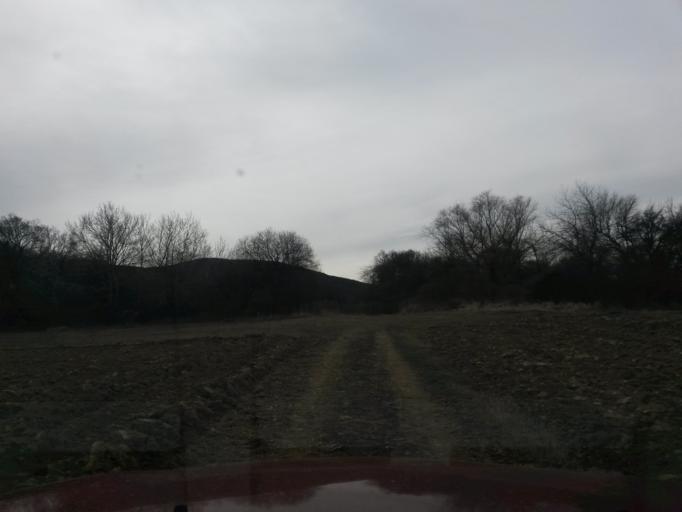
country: HU
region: Borsod-Abauj-Zemplen
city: Gonc
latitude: 48.5797
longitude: 21.3764
